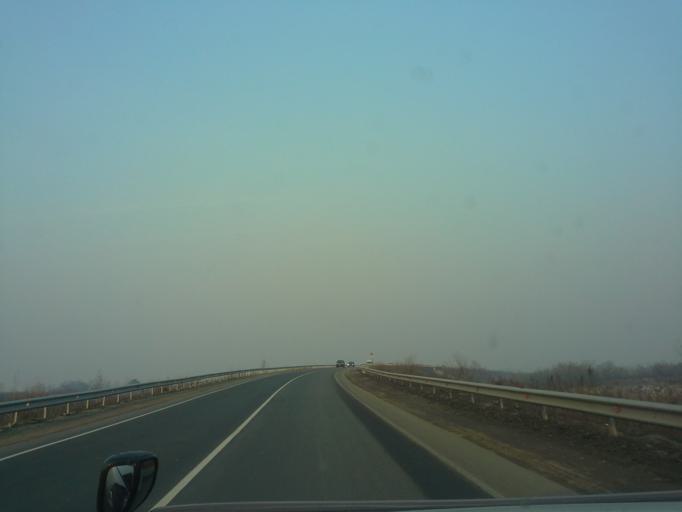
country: RU
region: Jewish Autonomous Oblast
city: Priamurskiy
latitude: 48.5198
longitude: 134.9136
